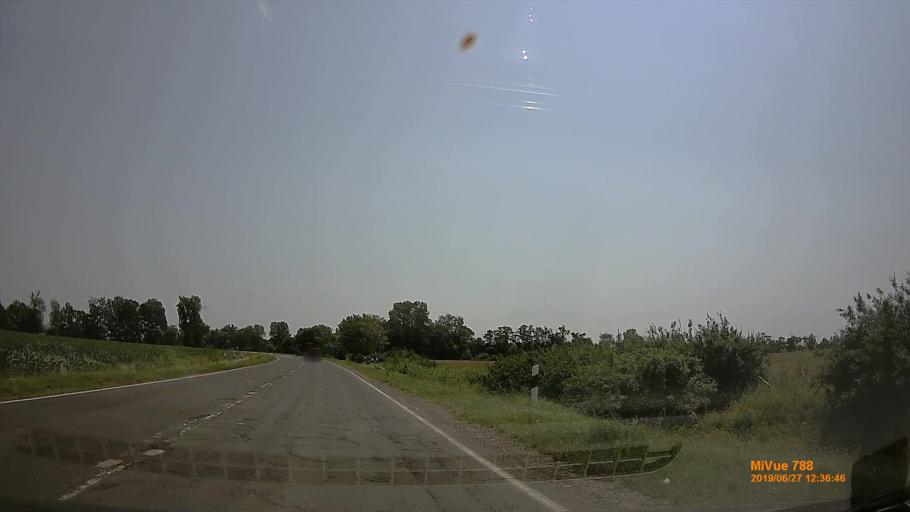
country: HU
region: Pest
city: Tortel
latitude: 47.1871
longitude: 19.9264
